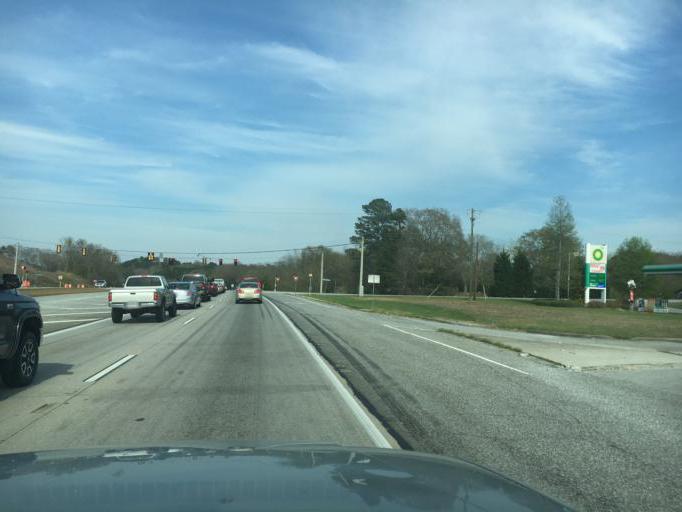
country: US
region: Georgia
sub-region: Hall County
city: Gainesville
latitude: 34.3490
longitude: -83.7601
